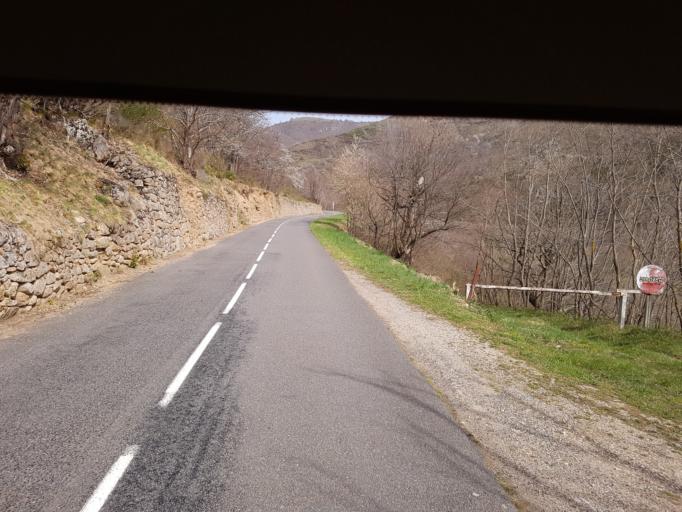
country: FR
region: Languedoc-Roussillon
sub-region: Departement de la Lozere
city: Florac
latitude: 44.3571
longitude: 3.6629
